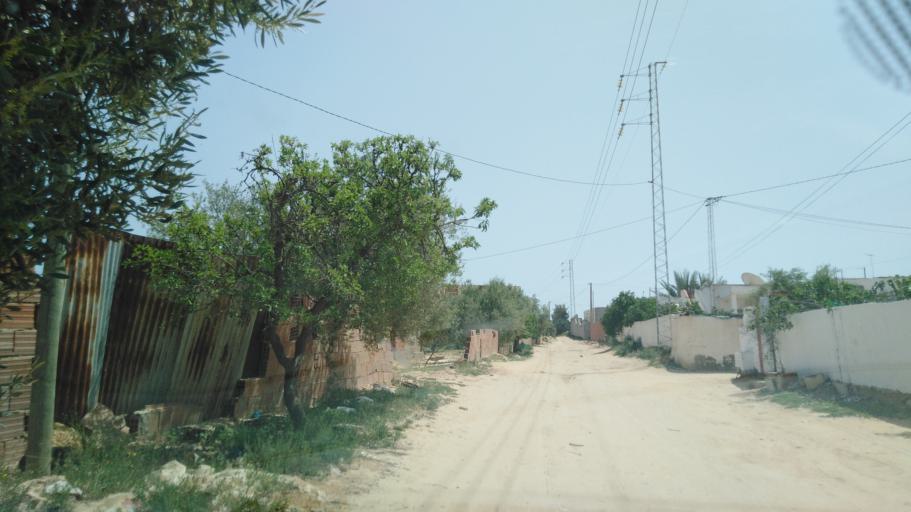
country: TN
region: Safaqis
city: Sfax
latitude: 34.7318
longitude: 10.5512
